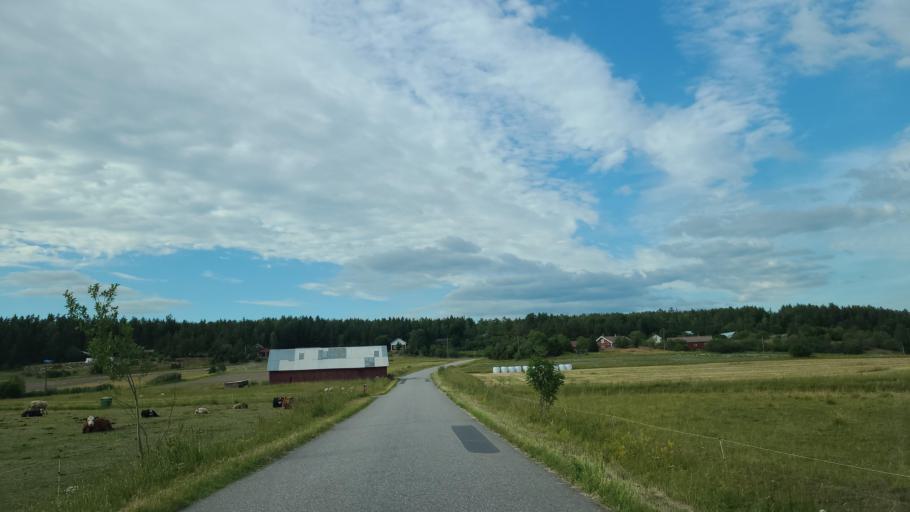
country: FI
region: Varsinais-Suomi
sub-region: Turku
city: Rymaettylae
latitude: 60.2957
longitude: 21.9370
